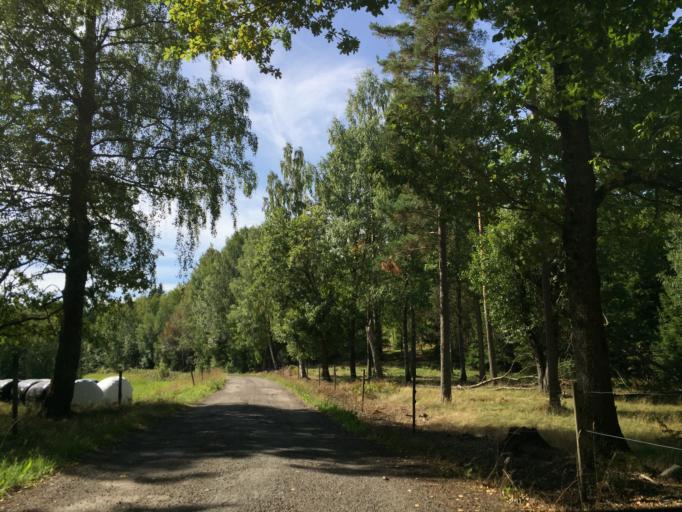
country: NO
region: Vestfold
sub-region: Hof
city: Hof
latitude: 59.4612
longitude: 10.1460
